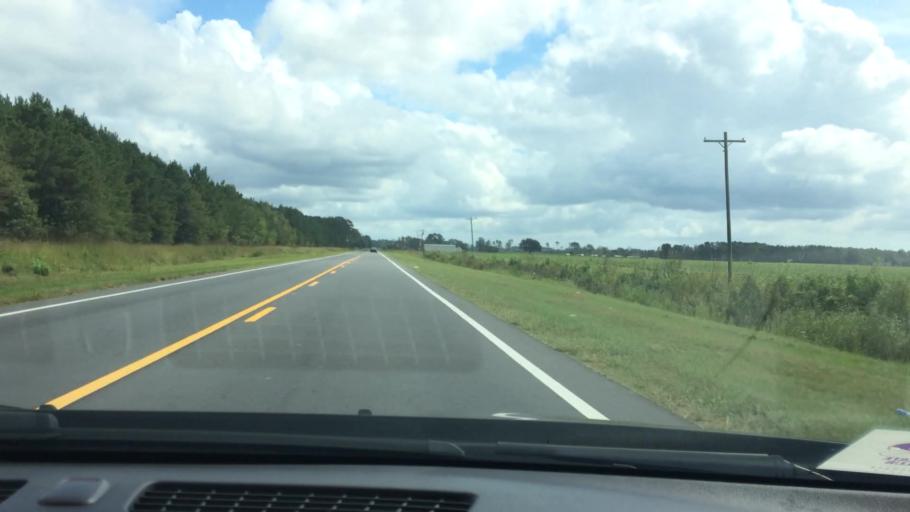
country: US
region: North Carolina
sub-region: Pitt County
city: Farmville
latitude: 35.5767
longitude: -77.5842
